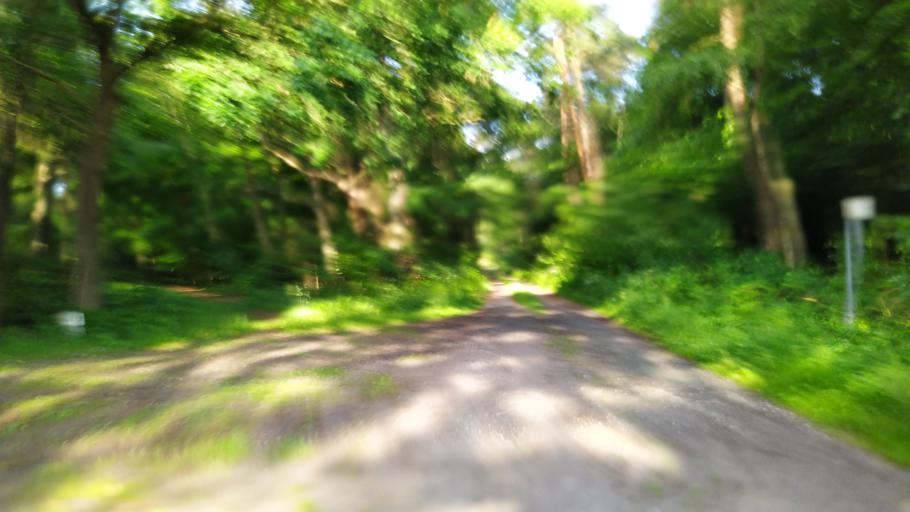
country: DE
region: Lower Saxony
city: Deinstedt
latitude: 53.4389
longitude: 9.2318
